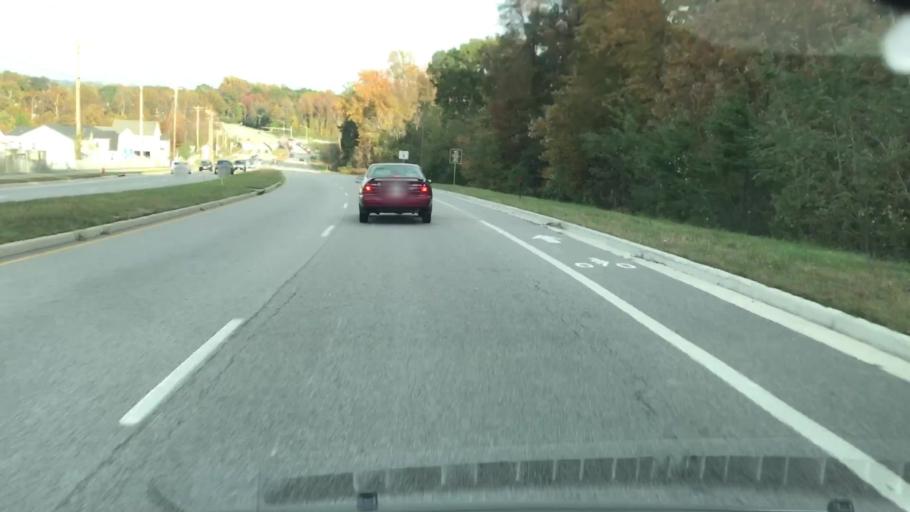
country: US
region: Virginia
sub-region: Fairfax County
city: Hayfield
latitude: 38.7429
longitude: -77.1563
